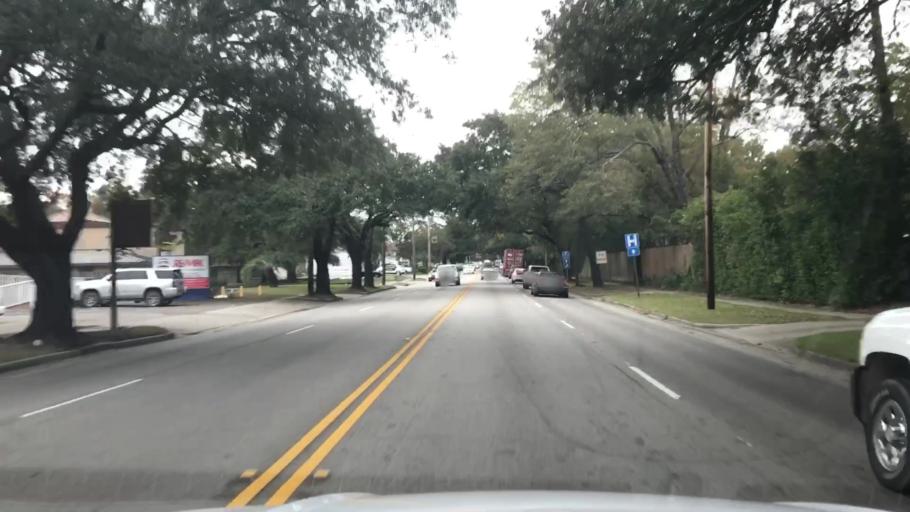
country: US
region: South Carolina
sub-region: Georgetown County
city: Georgetown
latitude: 33.3712
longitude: -79.2796
